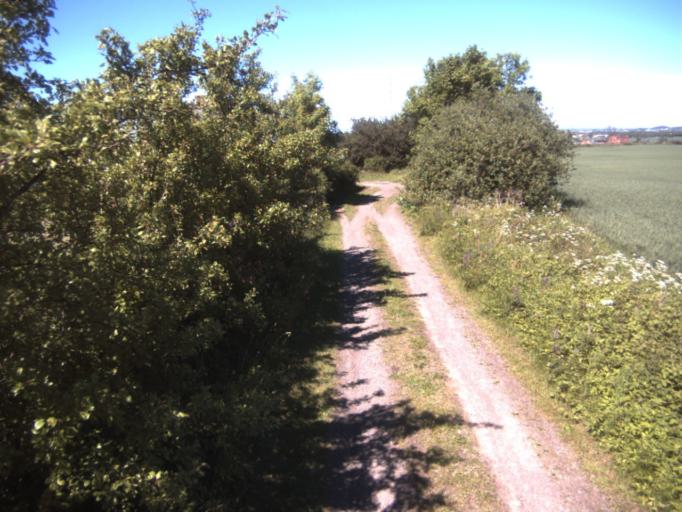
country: SE
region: Skane
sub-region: Helsingborg
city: Morarp
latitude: 56.0651
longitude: 12.8797
